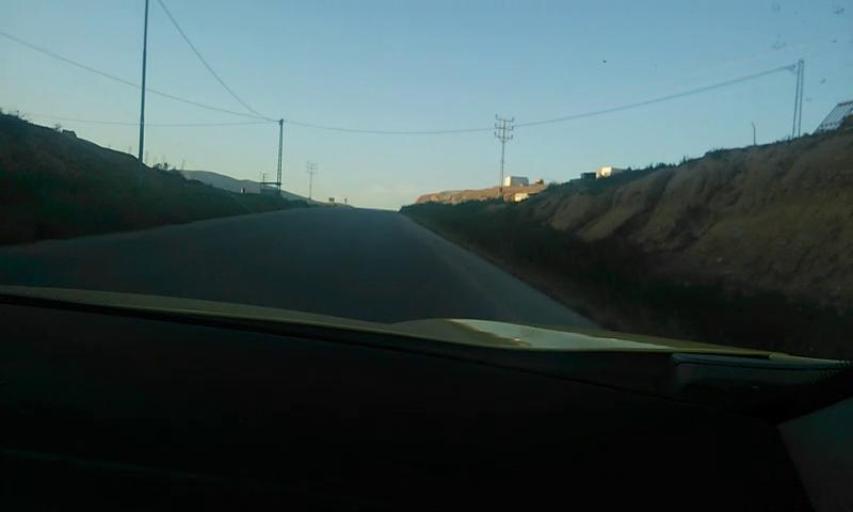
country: PS
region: West Bank
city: An Nuway`imah
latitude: 31.9027
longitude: 35.4254
